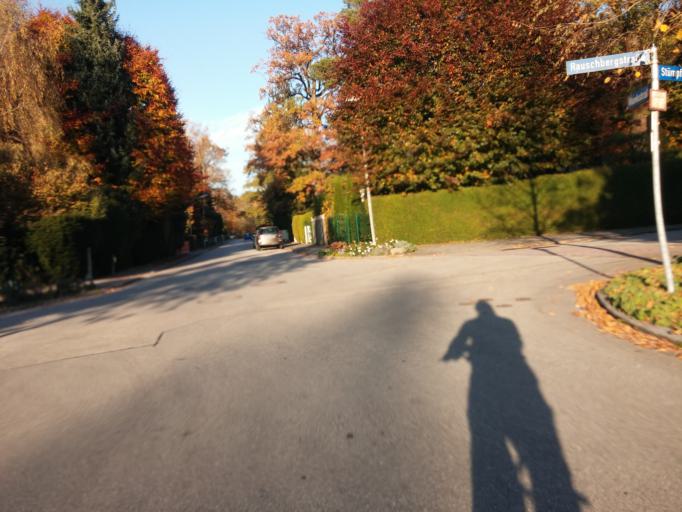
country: DE
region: Bavaria
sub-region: Upper Bavaria
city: Vaterstetten
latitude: 48.0926
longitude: 11.7942
